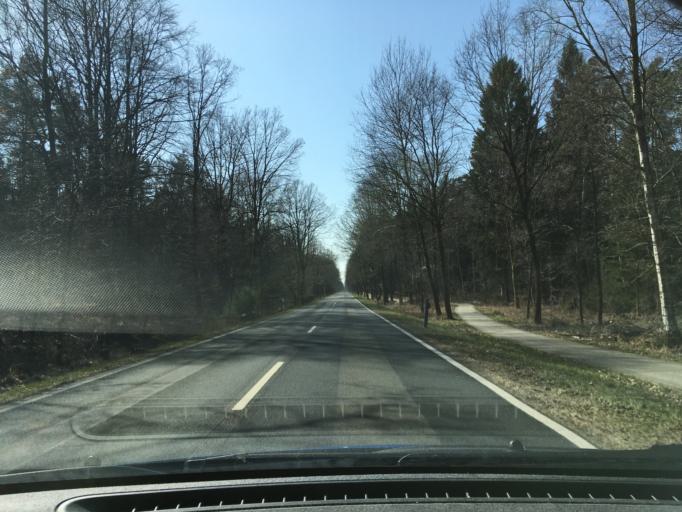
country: DE
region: Lower Saxony
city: Unterluss
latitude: 52.8318
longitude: 10.2706
